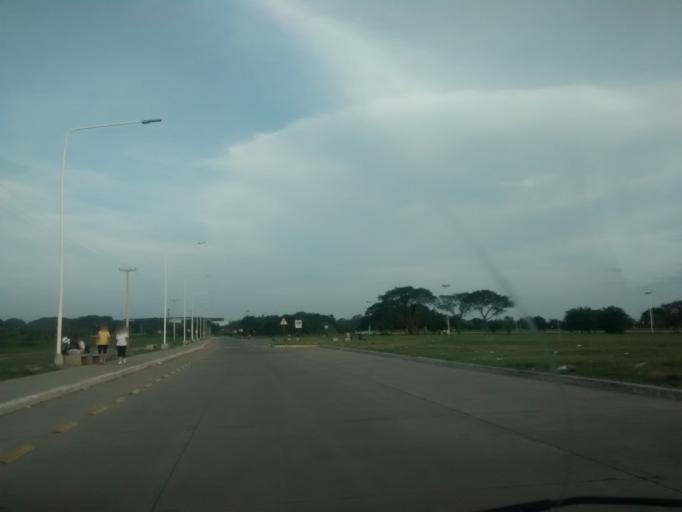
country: AR
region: Chaco
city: Resistencia
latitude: -27.4320
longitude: -58.9703
